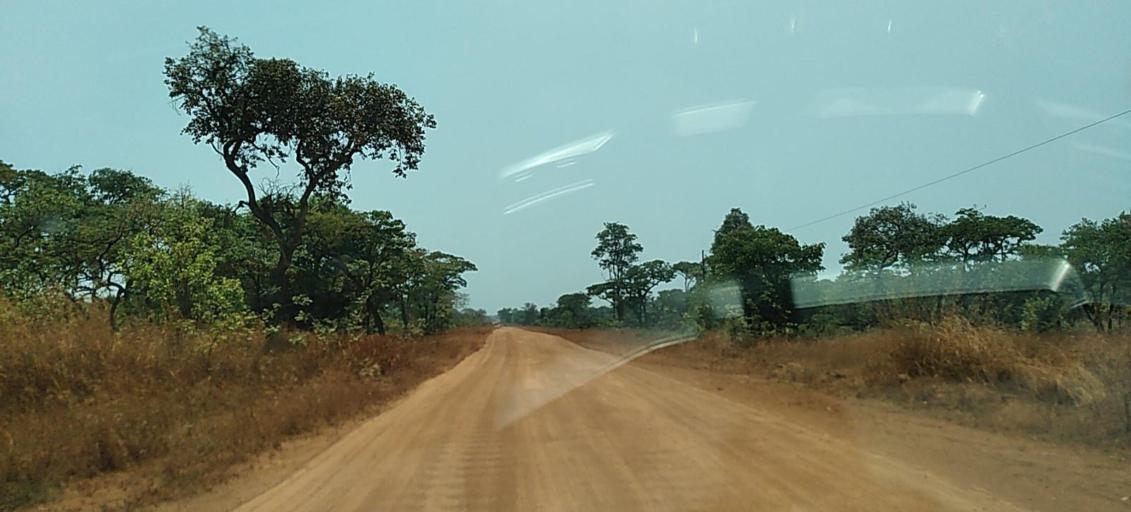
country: CD
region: Katanga
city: Kipushi
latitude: -11.9283
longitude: 26.9929
